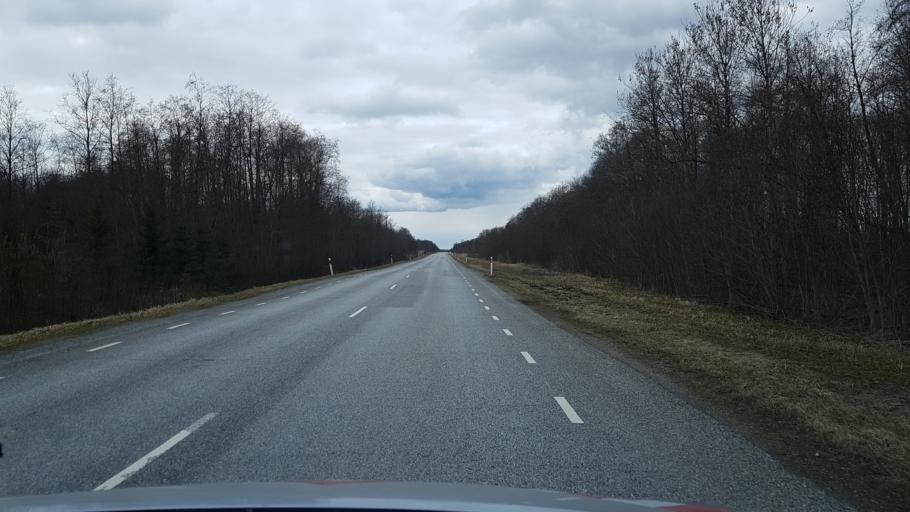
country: EE
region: Ida-Virumaa
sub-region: Narva-Joesuu linn
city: Narva-Joesuu
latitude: 59.3377
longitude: 27.9736
